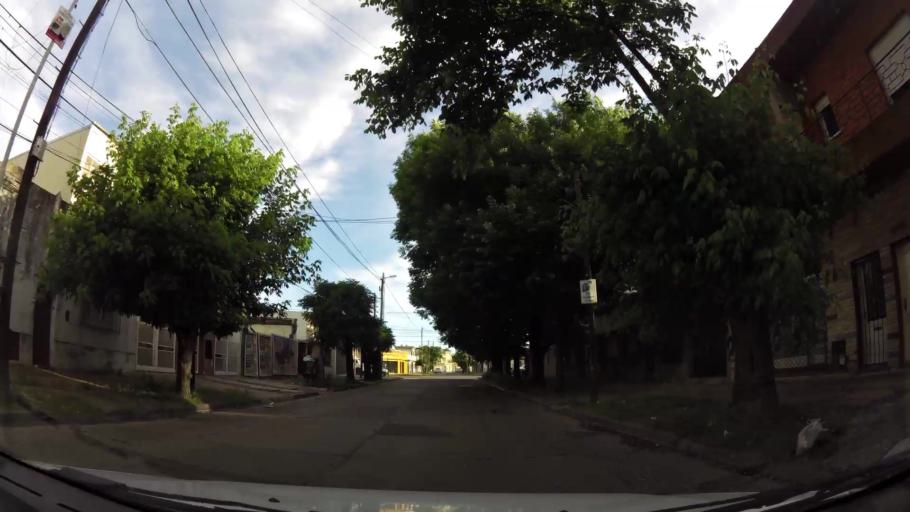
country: AR
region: Buenos Aires
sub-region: Partido de Moron
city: Moron
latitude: -34.6598
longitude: -58.6186
